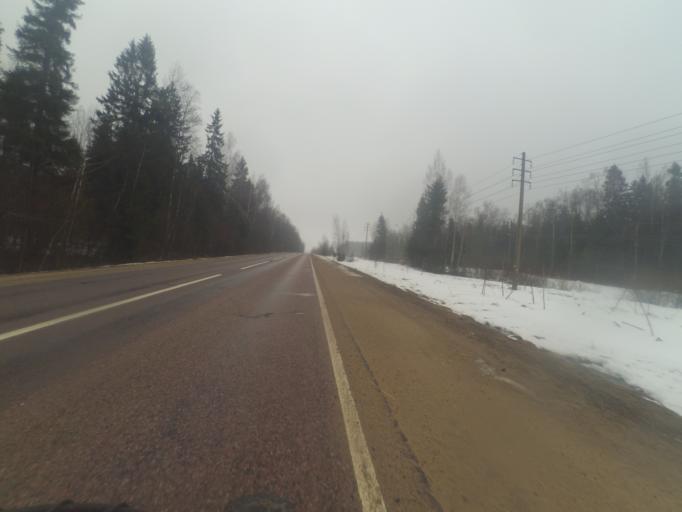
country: RU
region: Moskovskaya
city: Avtopoligon
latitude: 56.2654
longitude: 37.3179
